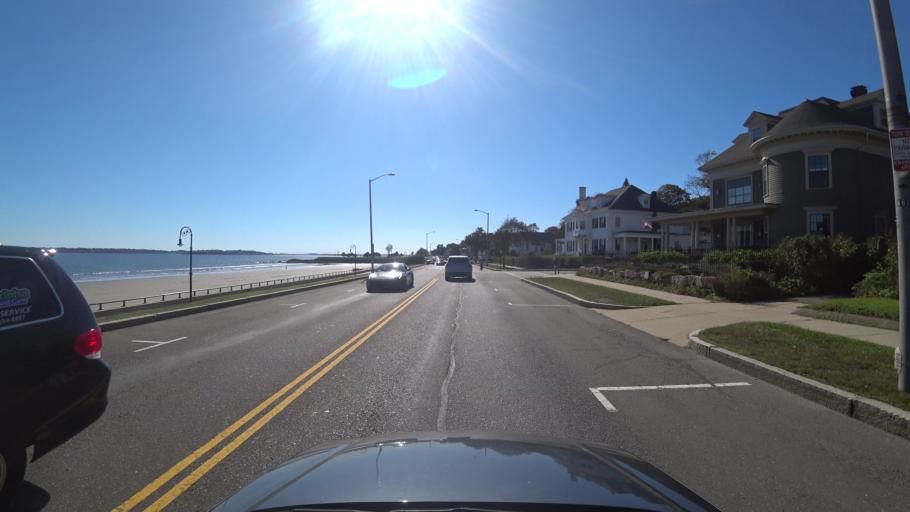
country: US
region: Massachusetts
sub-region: Essex County
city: Swampscott
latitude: 42.4654
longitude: -70.9246
